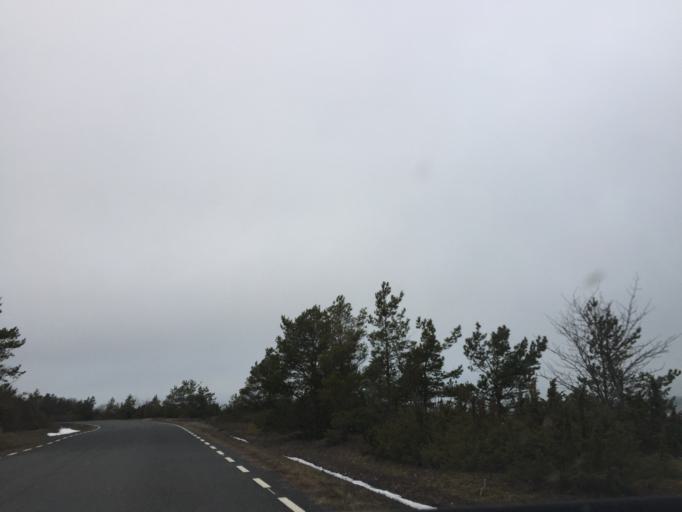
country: EE
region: Saare
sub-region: Kuressaare linn
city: Kuressaare
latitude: 58.5656
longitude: 22.3099
